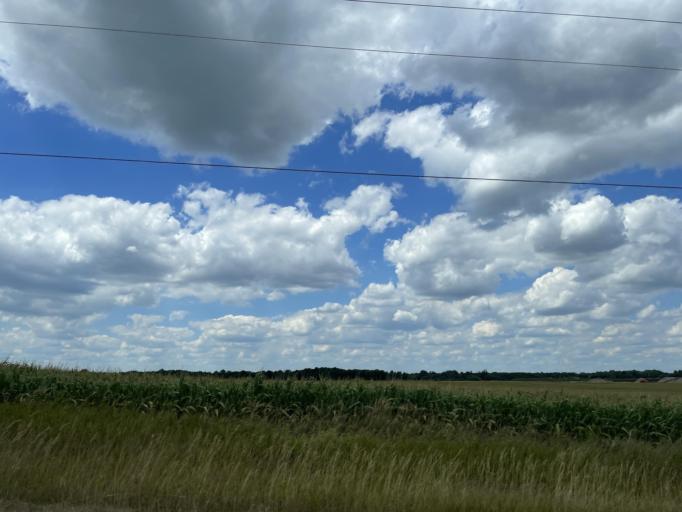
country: CA
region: Ontario
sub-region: Wellington County
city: Guelph
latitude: 43.5391
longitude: -80.3638
